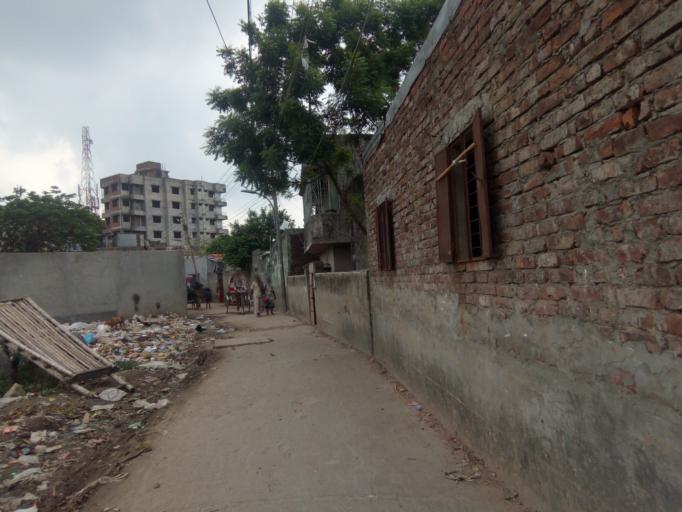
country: BD
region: Dhaka
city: Paltan
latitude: 23.7548
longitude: 90.4357
